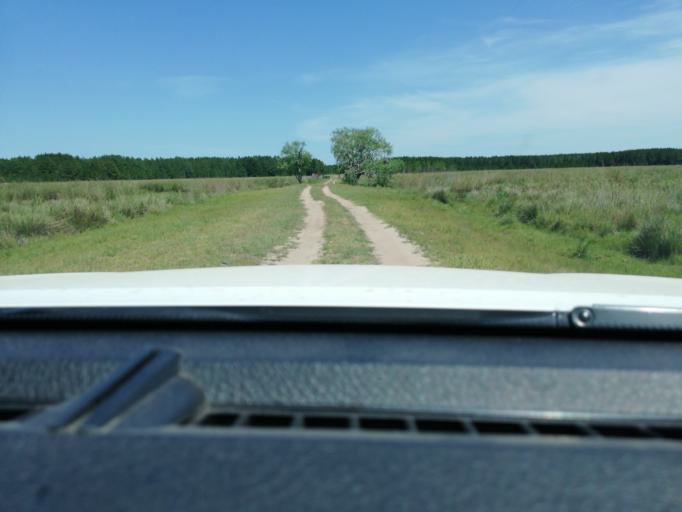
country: AR
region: Corrientes
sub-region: Departamento de San Miguel
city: San Miguel
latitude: -28.0302
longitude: -57.4708
